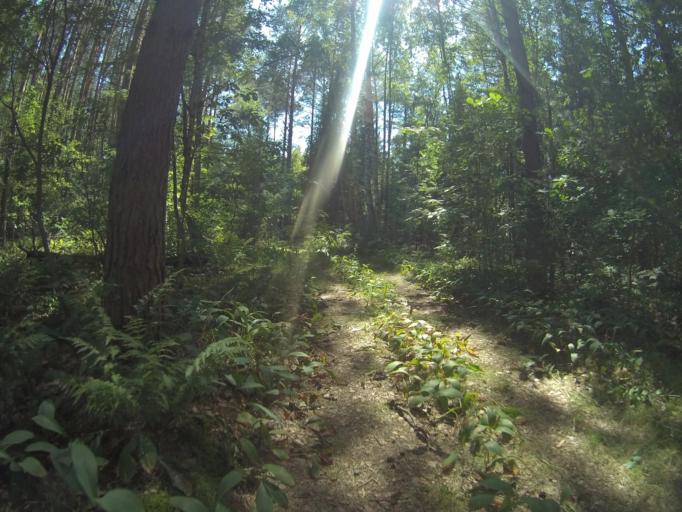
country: RU
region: Vladimir
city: Raduzhnyy
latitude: 56.0220
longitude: 40.2619
